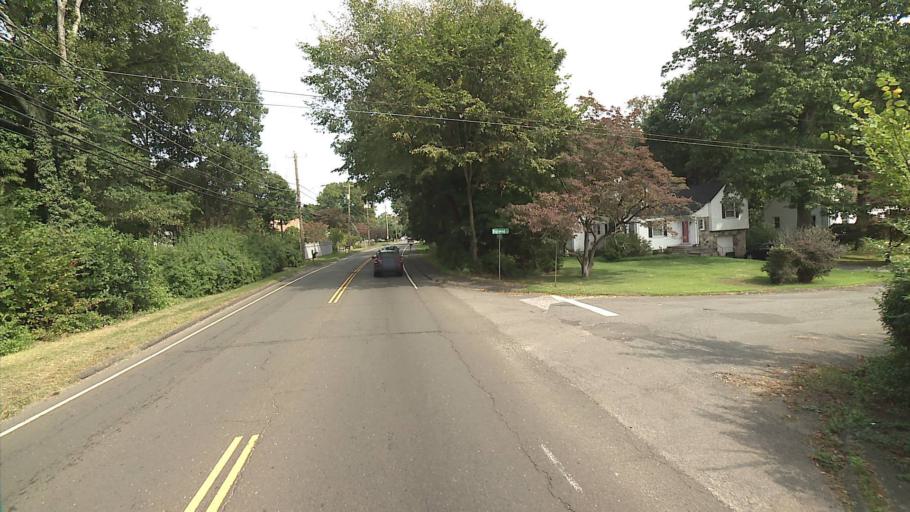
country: US
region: Connecticut
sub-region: Fairfield County
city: North Stamford
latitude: 41.1163
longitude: -73.5451
